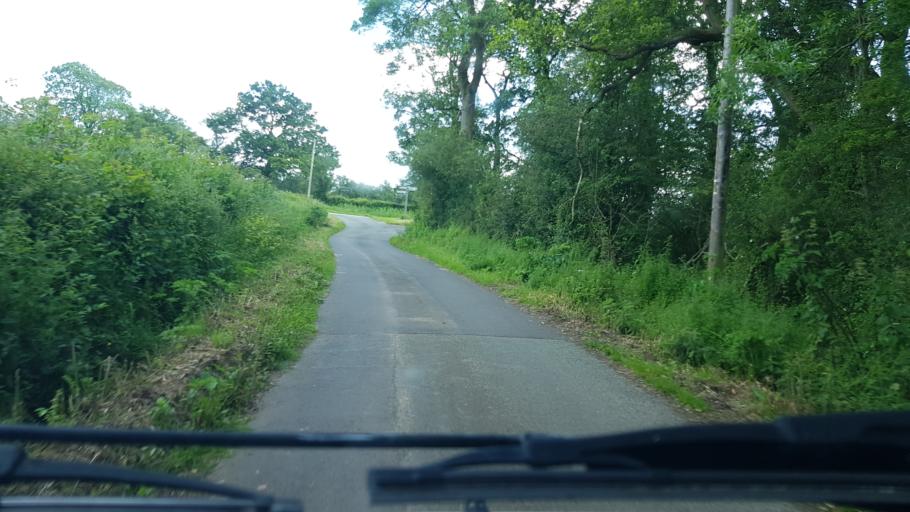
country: GB
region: England
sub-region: Shropshire
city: Romsley
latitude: 52.4476
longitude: -2.3074
